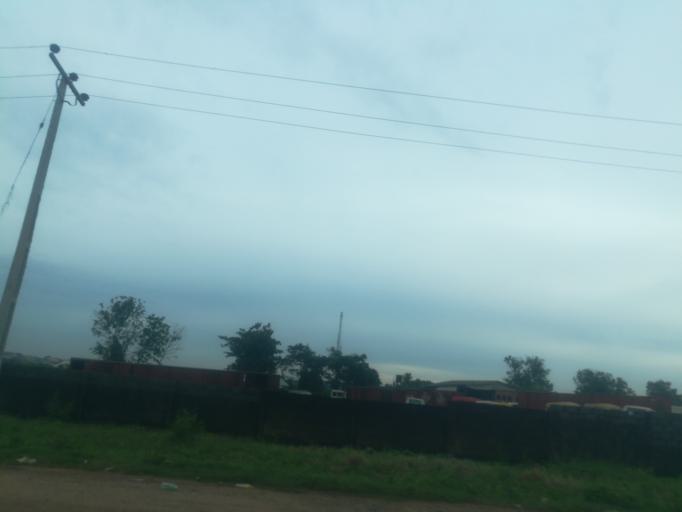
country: NG
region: Oyo
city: Egbeda
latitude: 7.3826
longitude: 4.0170
